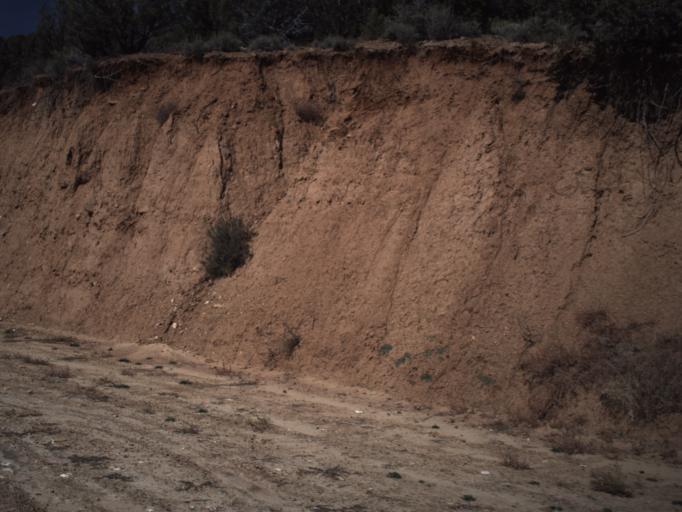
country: US
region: Utah
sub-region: Washington County
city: Enterprise
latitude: 37.5395
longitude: -113.6569
